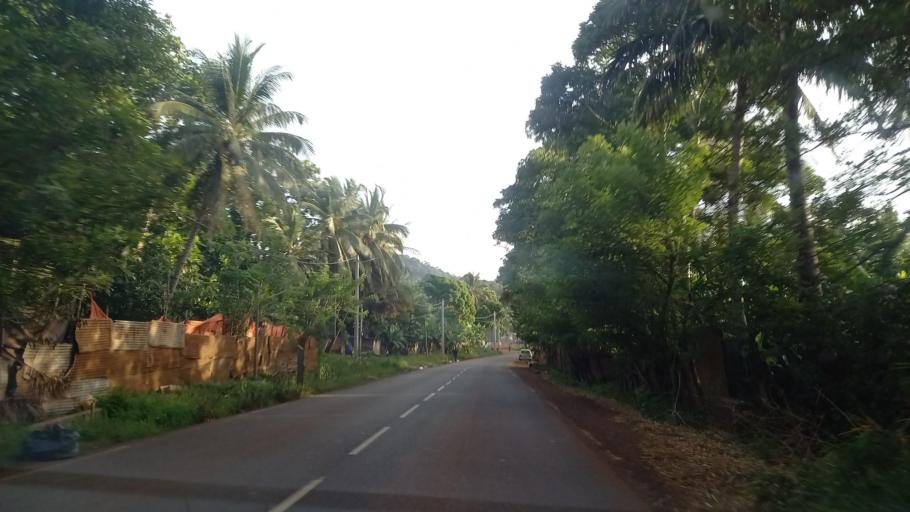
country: YT
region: Koungou
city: Koungou
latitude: -12.7309
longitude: 45.1622
